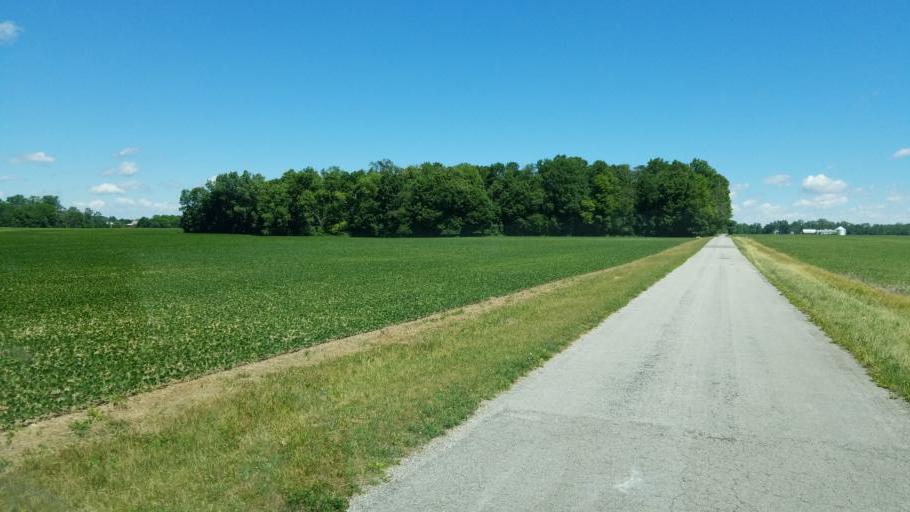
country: US
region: Ohio
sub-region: Morrow County
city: Cardington
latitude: 40.6198
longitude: -82.9427
